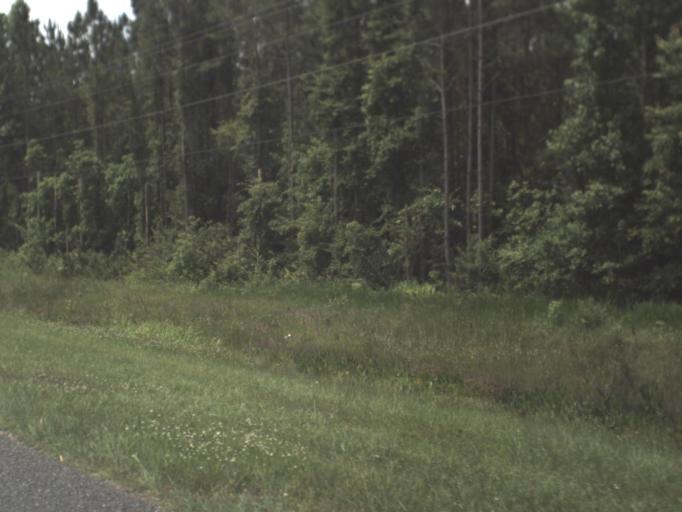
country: US
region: Florida
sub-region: Putnam County
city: East Palatka
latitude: 29.7983
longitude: -81.6531
